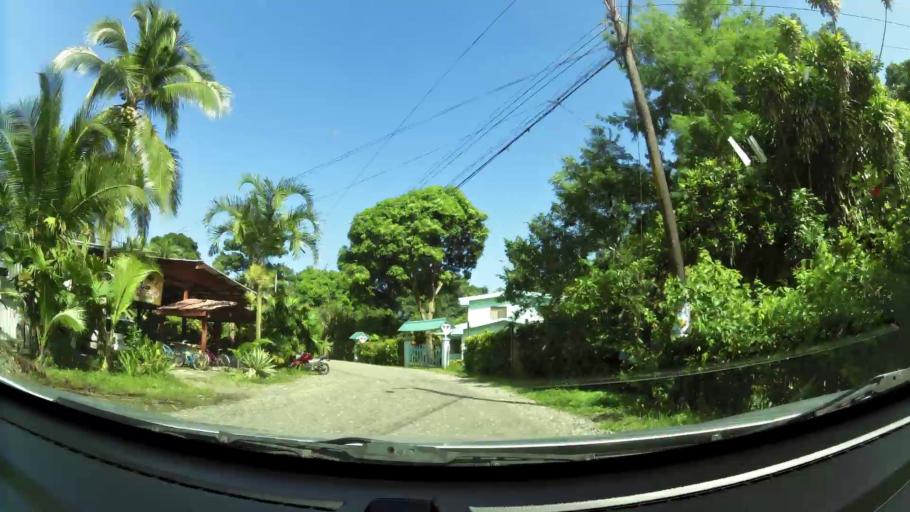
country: PA
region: Bocas del Toro
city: Barranco
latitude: 9.6403
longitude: -82.6902
